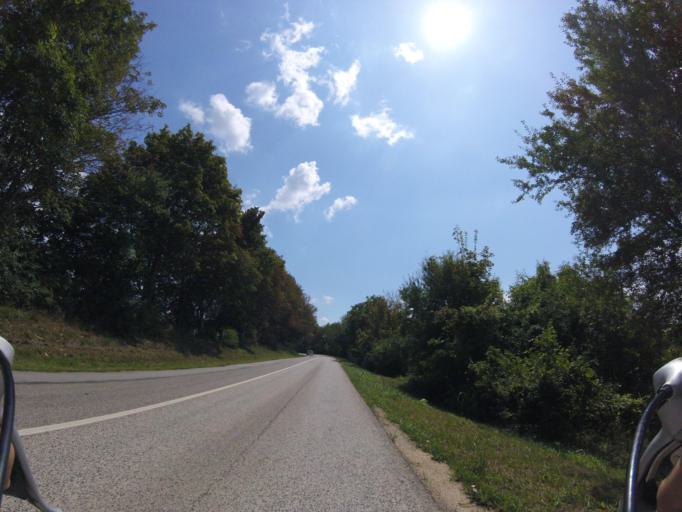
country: HU
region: Fejer
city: Etyek
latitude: 47.4852
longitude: 18.7685
